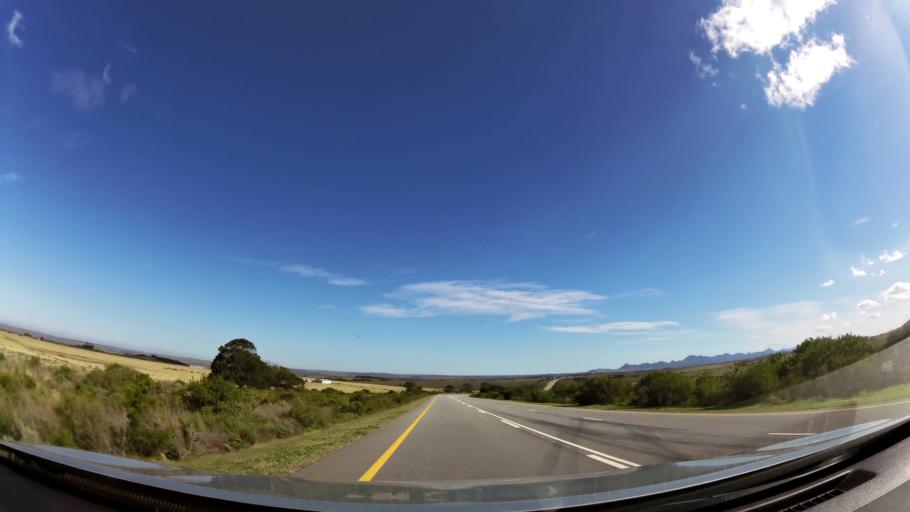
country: ZA
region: Eastern Cape
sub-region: Cacadu District Municipality
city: Kruisfontein
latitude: -34.0033
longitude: 24.6793
